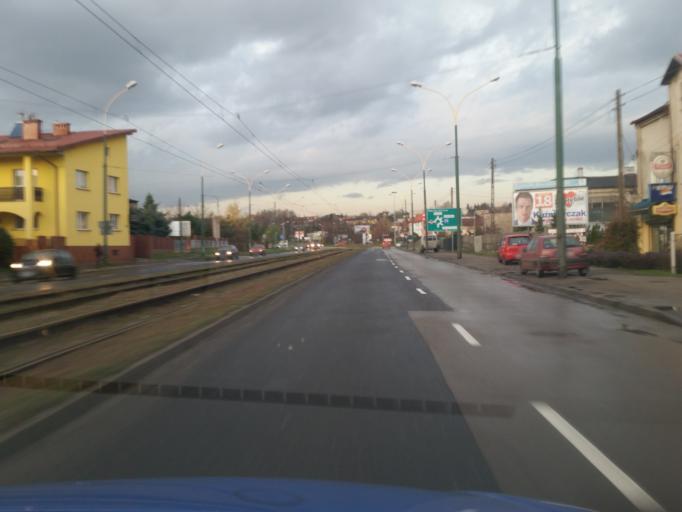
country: PL
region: Silesian Voivodeship
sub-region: Myslowice
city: Myslowice
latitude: 50.2704
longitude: 19.1770
